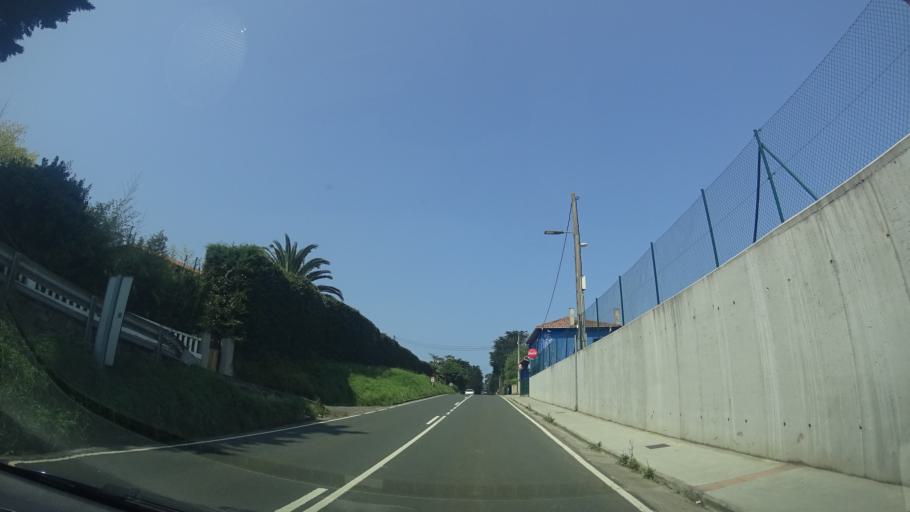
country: ES
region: Asturias
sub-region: Province of Asturias
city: Colunga
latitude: 43.4751
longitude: -5.2205
